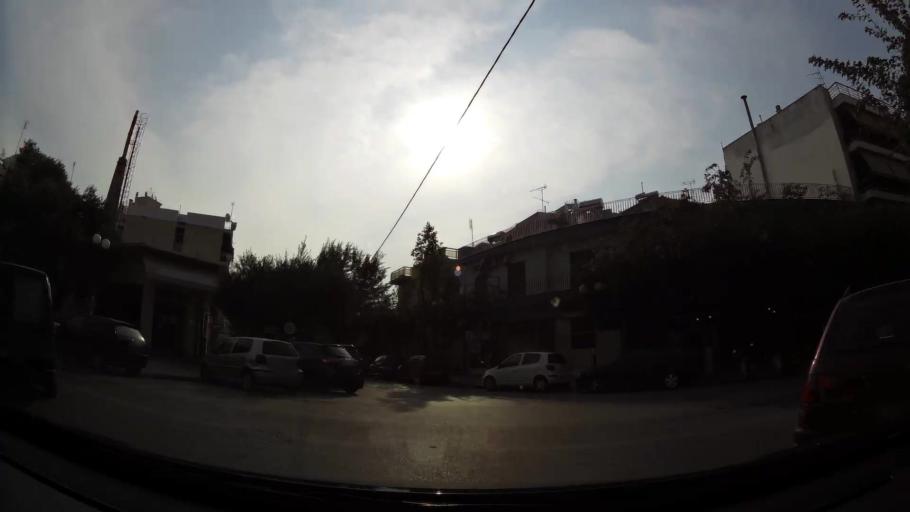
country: GR
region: Attica
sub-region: Nomarchia Athinas
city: Kallithea
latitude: 37.9529
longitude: 23.6910
